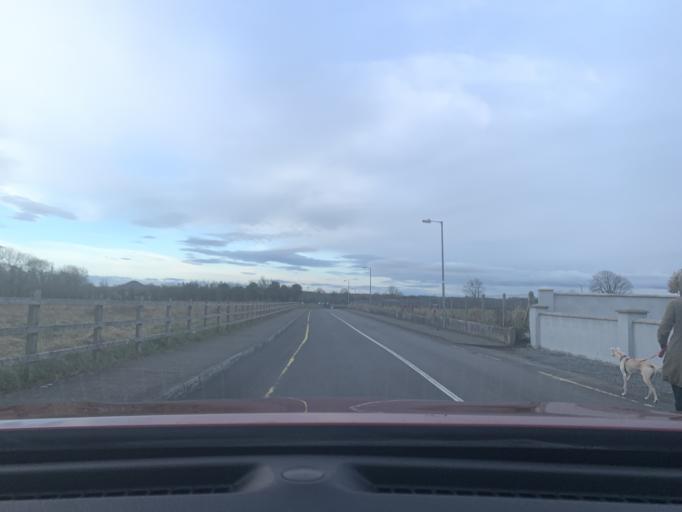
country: IE
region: Connaught
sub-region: Roscommon
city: Ballaghaderreen
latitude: 53.8989
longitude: -8.5919
